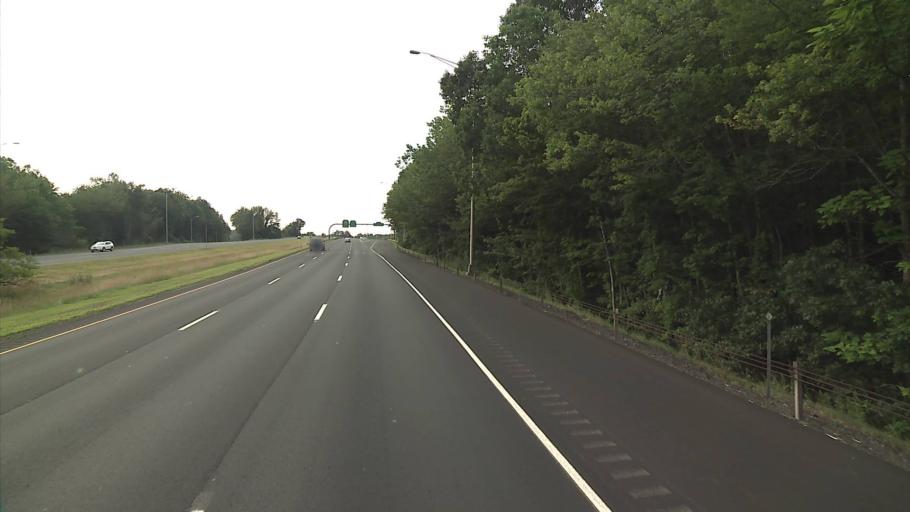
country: US
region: Connecticut
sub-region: New Haven County
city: Wolcott
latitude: 41.5901
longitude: -72.9021
